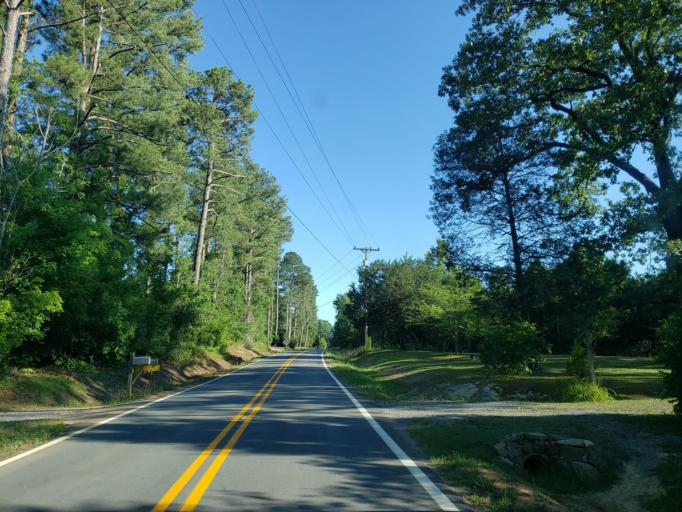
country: US
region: Georgia
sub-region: Floyd County
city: Shannon
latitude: 34.4618
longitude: -85.1154
